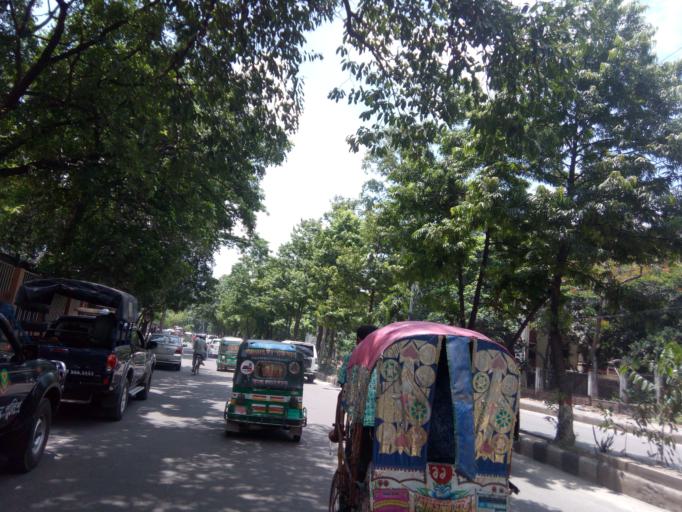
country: BD
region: Dhaka
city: Paltan
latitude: 23.7425
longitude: 90.4057
